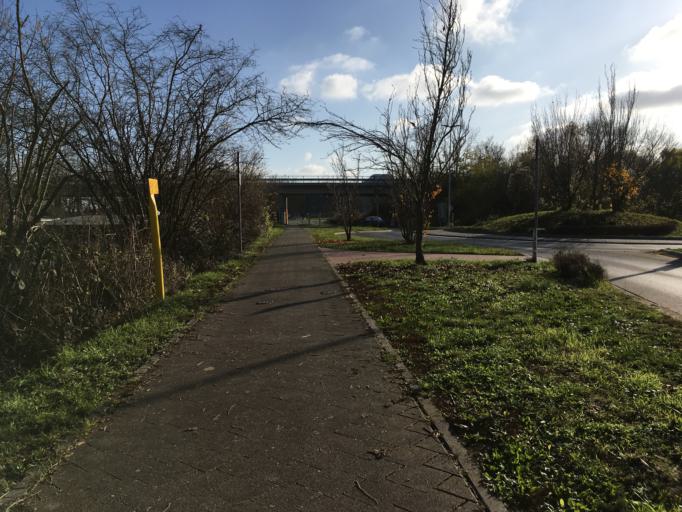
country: DE
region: Rheinland-Pfalz
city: Bodenheim
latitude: 49.9239
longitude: 8.3194
